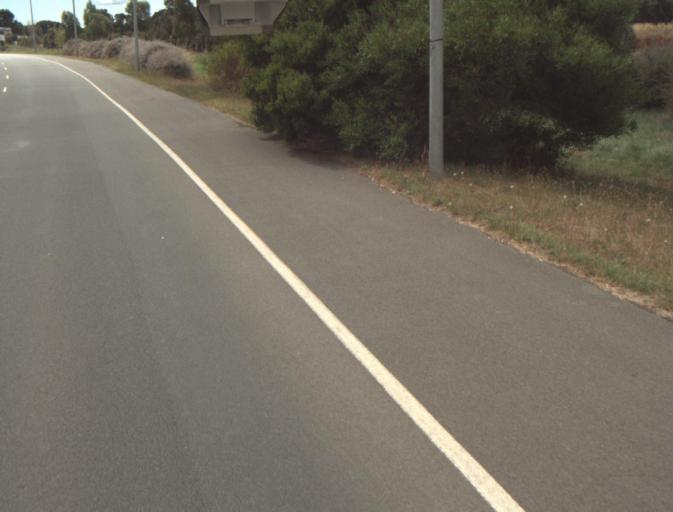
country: AU
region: Tasmania
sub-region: Launceston
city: Launceston
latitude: -41.4288
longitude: 147.1195
